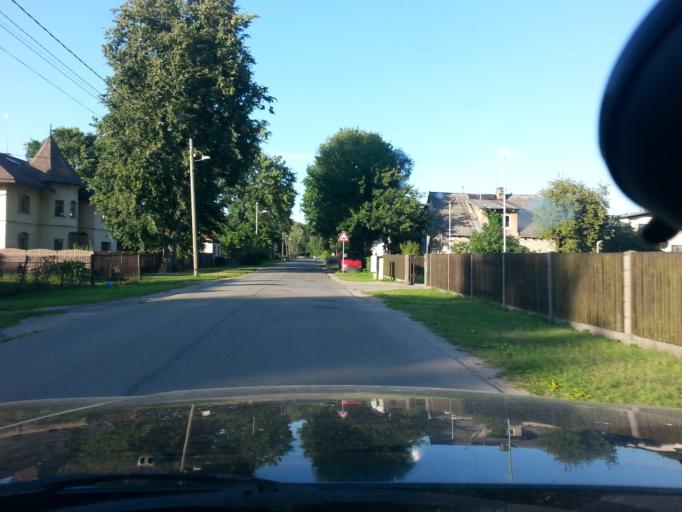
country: LV
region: Riga
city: Riga
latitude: 56.9413
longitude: 24.1915
